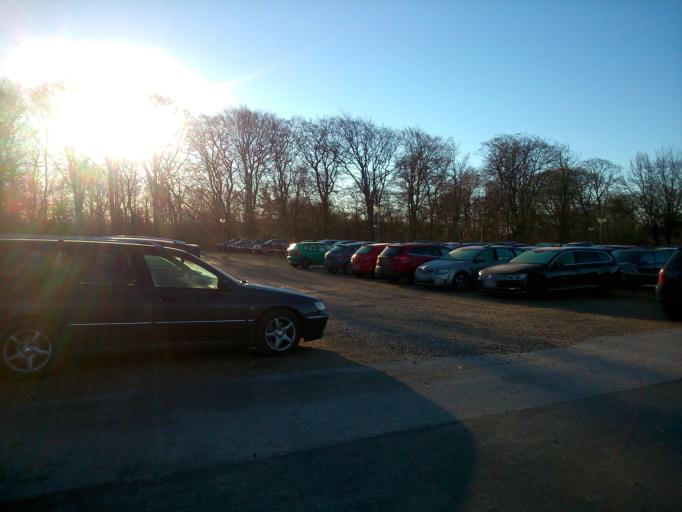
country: DK
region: Central Jutland
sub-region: Holstebro Kommune
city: Holstebro
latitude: 56.3626
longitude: 8.6285
